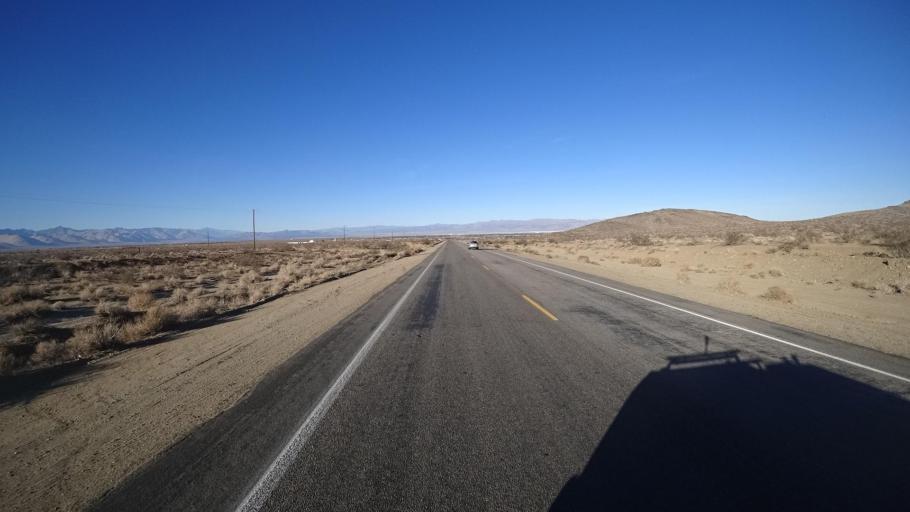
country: US
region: California
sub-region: Kern County
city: Ridgecrest
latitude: 35.5717
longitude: -117.7139
